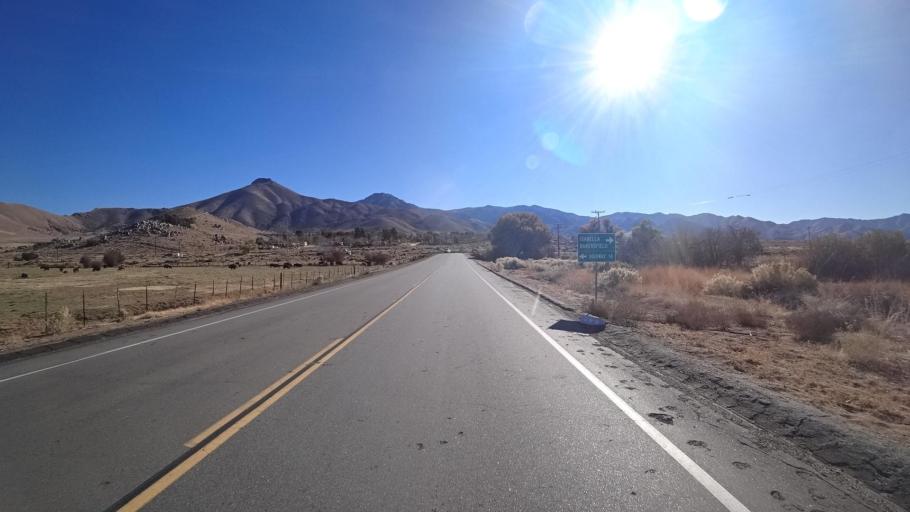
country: US
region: California
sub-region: Kern County
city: Weldon
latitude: 35.6582
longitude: -118.3231
